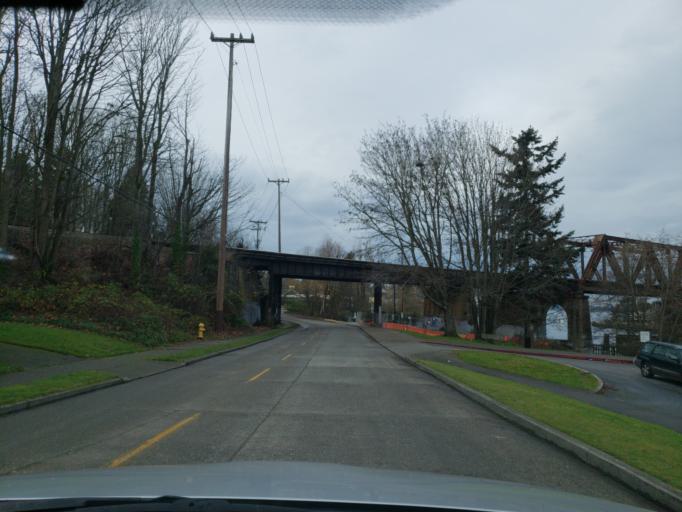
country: US
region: Washington
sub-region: King County
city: Seattle
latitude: 47.6654
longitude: -122.4012
